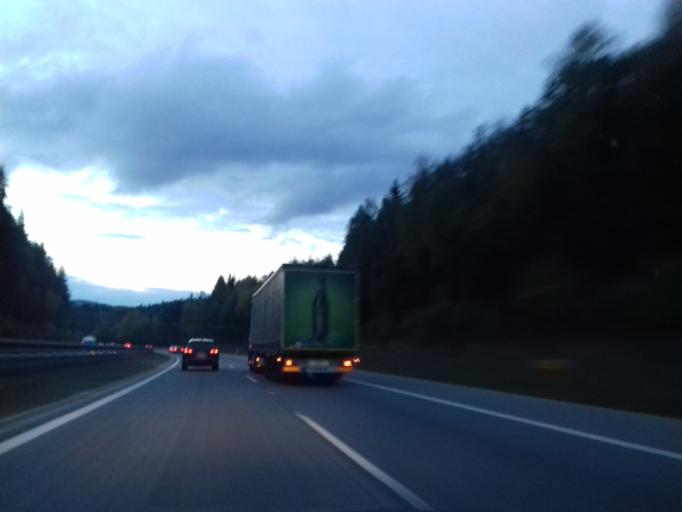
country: CZ
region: Central Bohemia
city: Divisov
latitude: 49.7655
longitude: 14.9506
